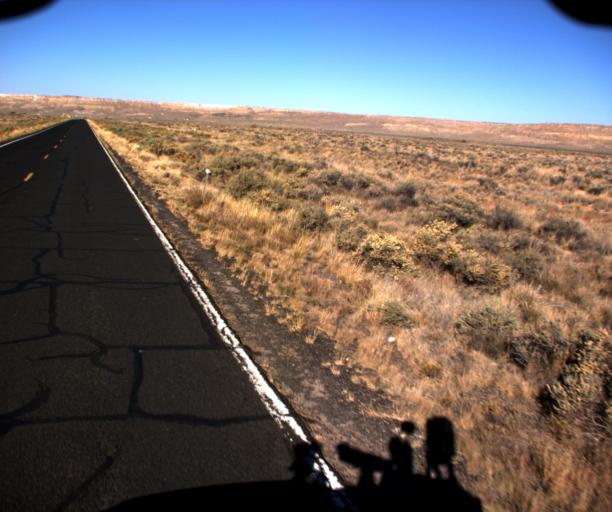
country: US
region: Arizona
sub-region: Navajo County
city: First Mesa
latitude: 35.8407
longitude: -110.3173
